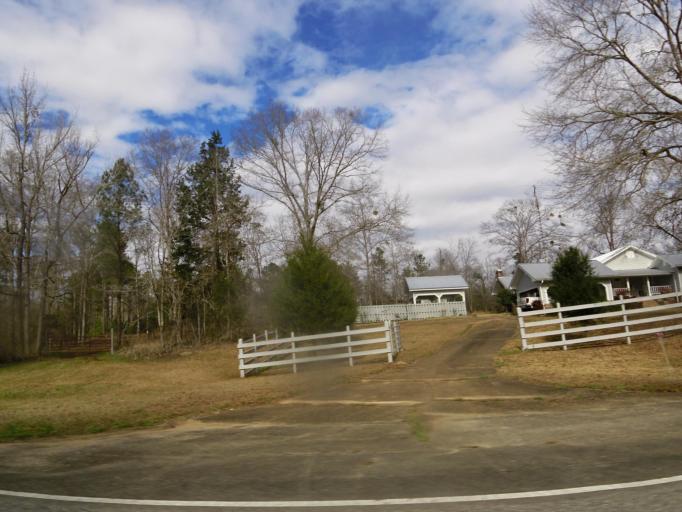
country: US
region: Alabama
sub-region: Barbour County
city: Eufaula
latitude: 31.9920
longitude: -85.2679
